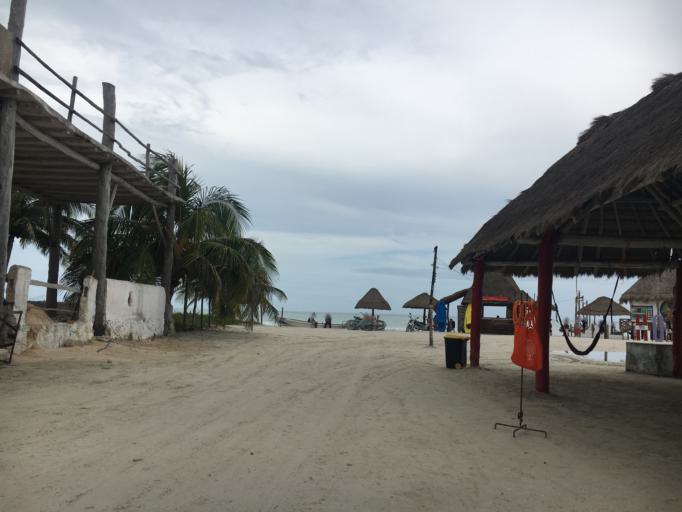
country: MX
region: Quintana Roo
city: Kantunilkin
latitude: 21.5248
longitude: -87.3796
